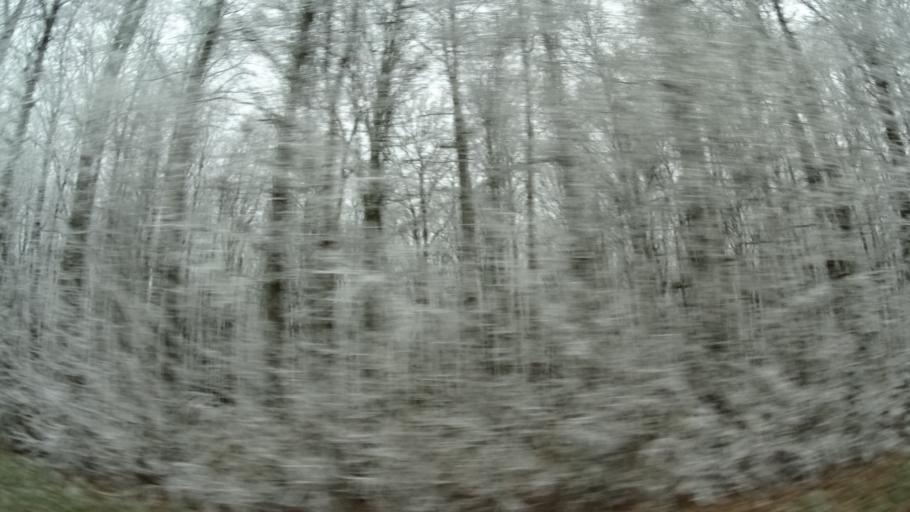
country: DE
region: Bavaria
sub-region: Regierungsbezirk Unterfranken
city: Hassfurt
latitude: 50.0209
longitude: 10.4951
